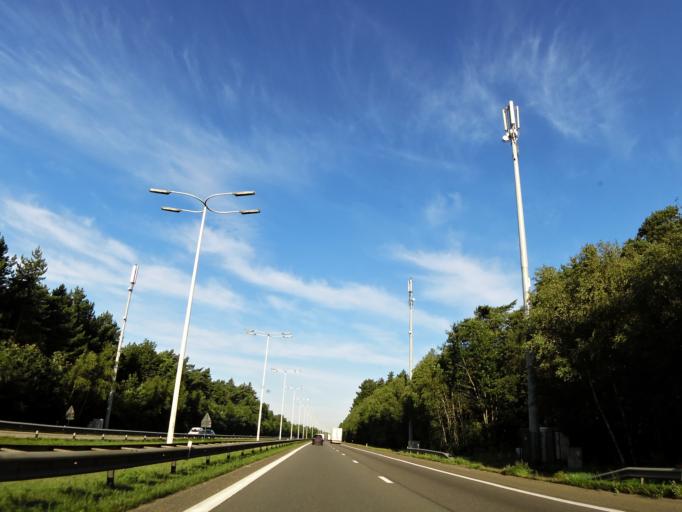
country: BE
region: Flanders
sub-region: Provincie Limburg
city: Zutendaal
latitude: 50.9633
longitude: 5.6135
